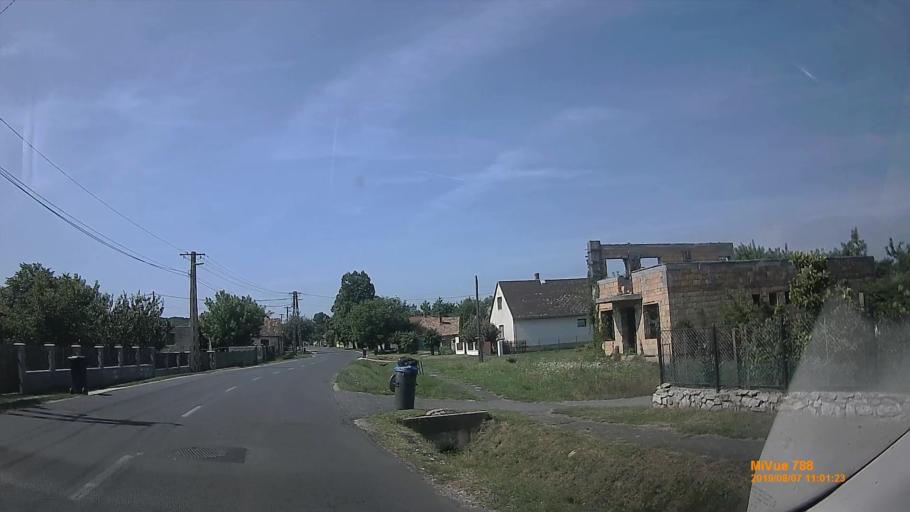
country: HU
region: Veszprem
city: Ajka
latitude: 47.0353
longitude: 17.5361
